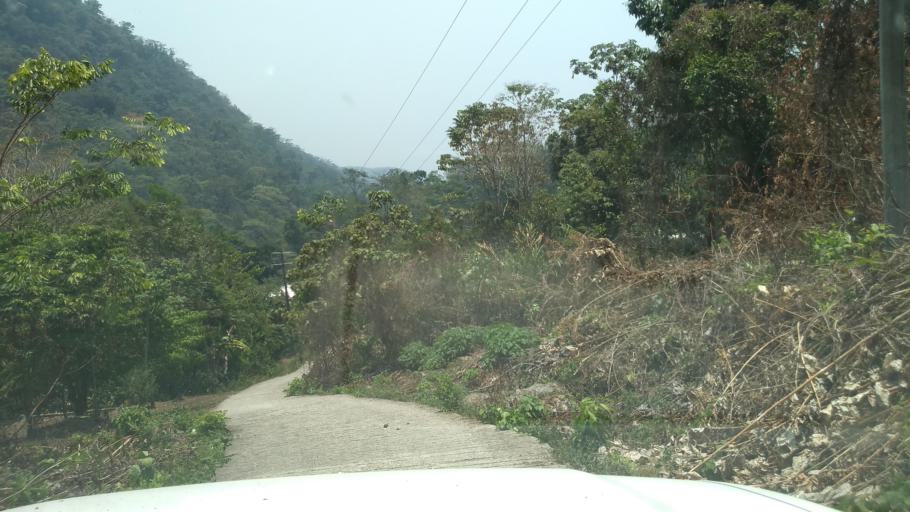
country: MX
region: Veracruz
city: Motzorongo
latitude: 18.6003
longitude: -96.7478
